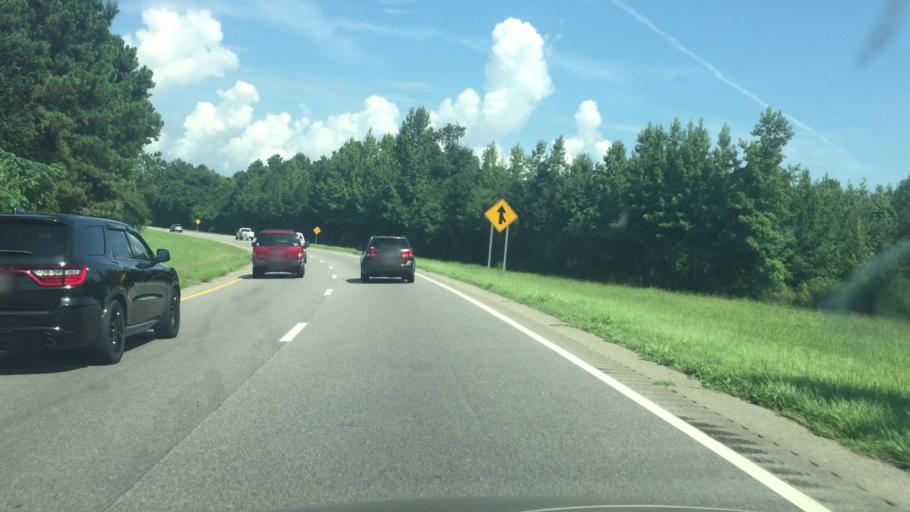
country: US
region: North Carolina
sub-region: Scotland County
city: Laurinburg
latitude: 34.7878
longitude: -79.5044
